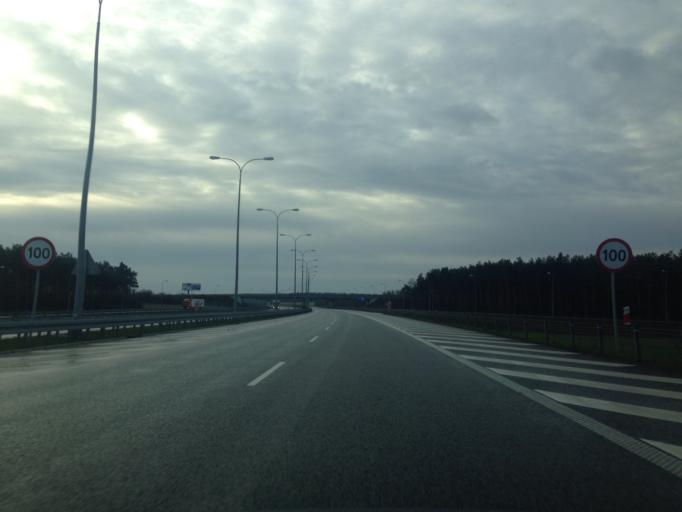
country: PL
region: Kujawsko-Pomorskie
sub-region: Powiat torunski
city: Lubicz Dolny
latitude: 53.0364
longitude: 18.7321
